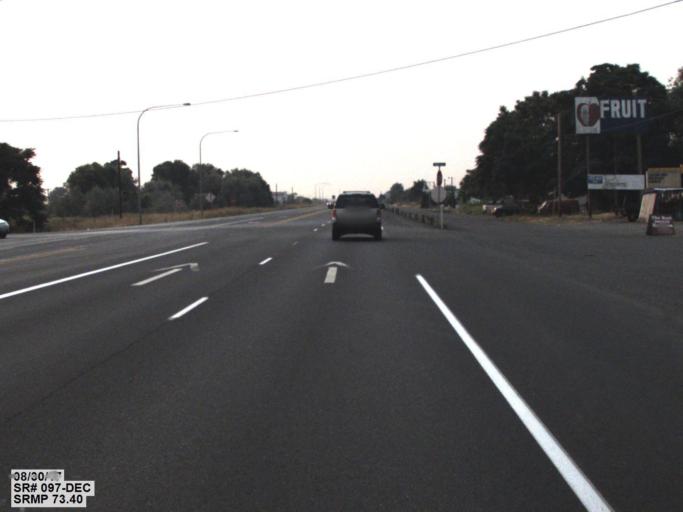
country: US
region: Washington
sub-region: Yakima County
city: Union Gap
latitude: 46.5039
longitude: -120.4675
